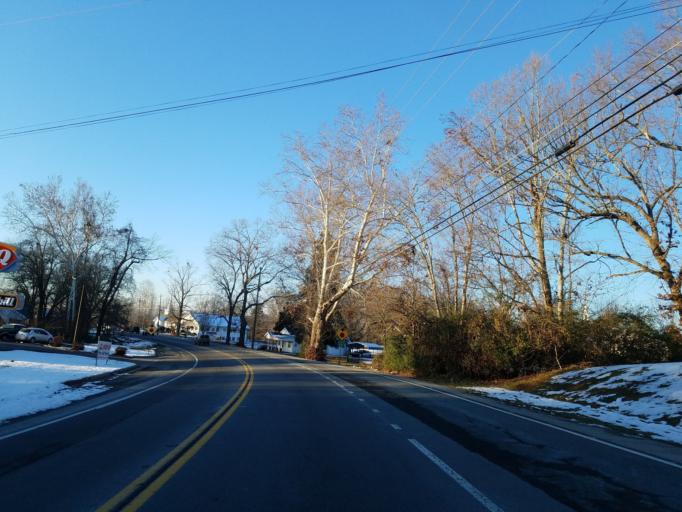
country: US
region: Georgia
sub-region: Dawson County
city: Dawsonville
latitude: 34.4195
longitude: -84.1144
